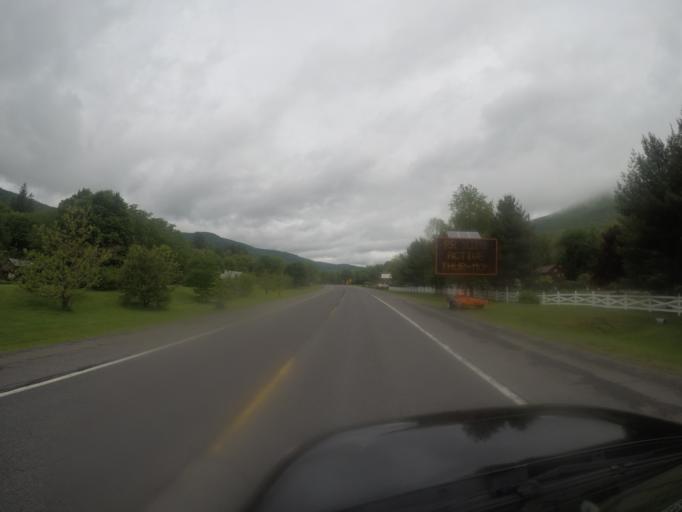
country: US
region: New York
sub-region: Ulster County
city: Shokan
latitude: 42.0506
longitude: -74.2892
